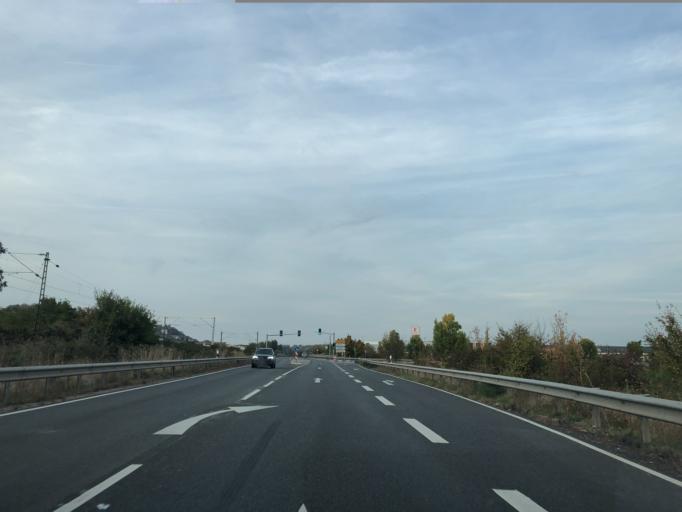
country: DE
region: Rheinland-Pfalz
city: Dienheim
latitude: 49.8440
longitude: 8.3581
